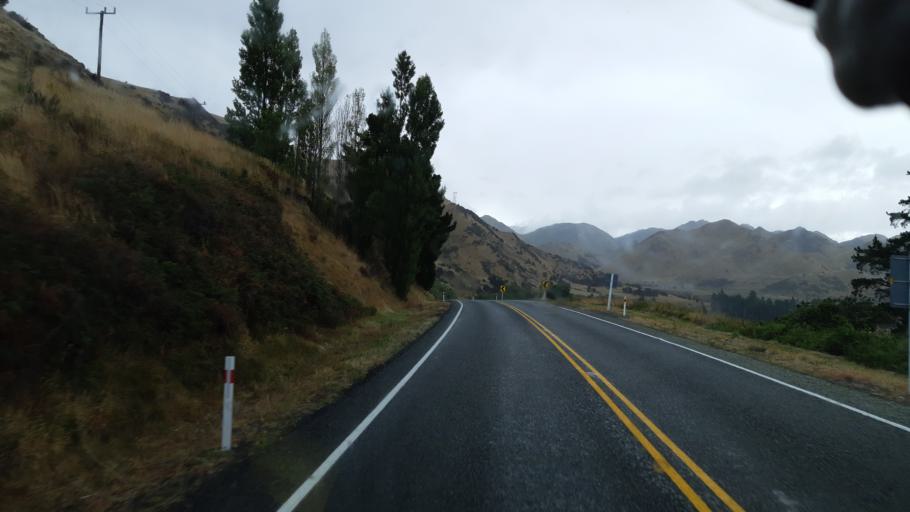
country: NZ
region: Canterbury
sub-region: Hurunui District
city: Amberley
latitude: -42.6712
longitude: 172.7724
